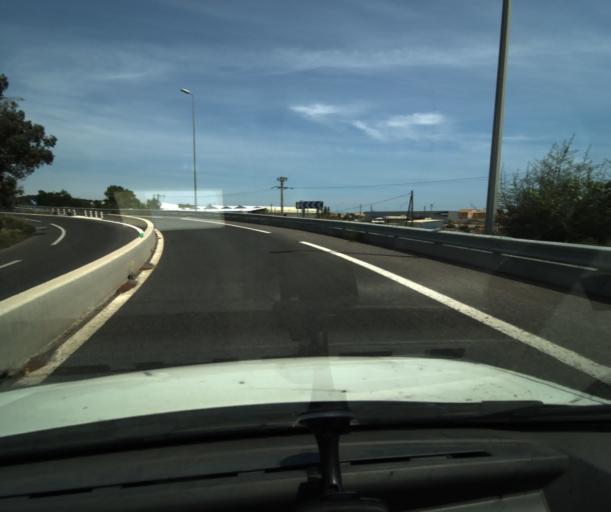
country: FR
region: Languedoc-Roussillon
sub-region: Departement des Pyrenees-Orientales
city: el Volo
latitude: 42.5255
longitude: 2.8218
